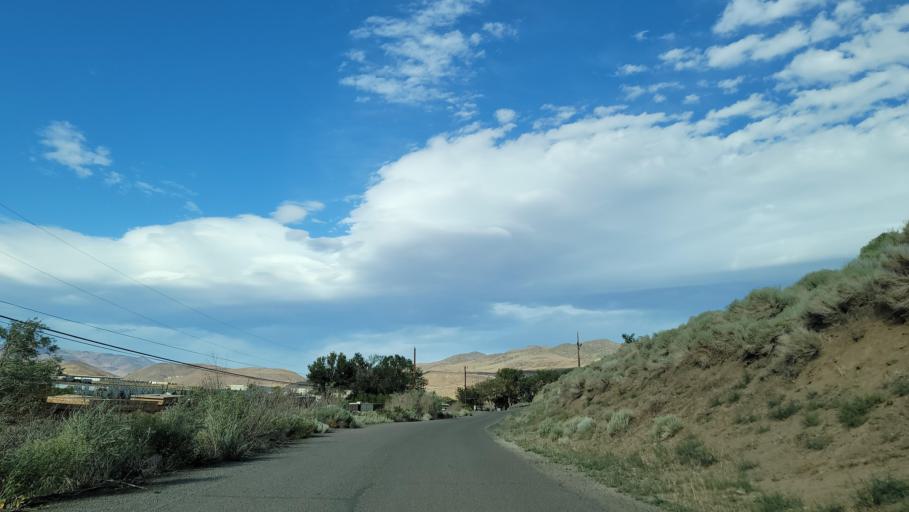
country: US
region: Nevada
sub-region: Washoe County
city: Sparks
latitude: 39.5095
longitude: -119.6361
